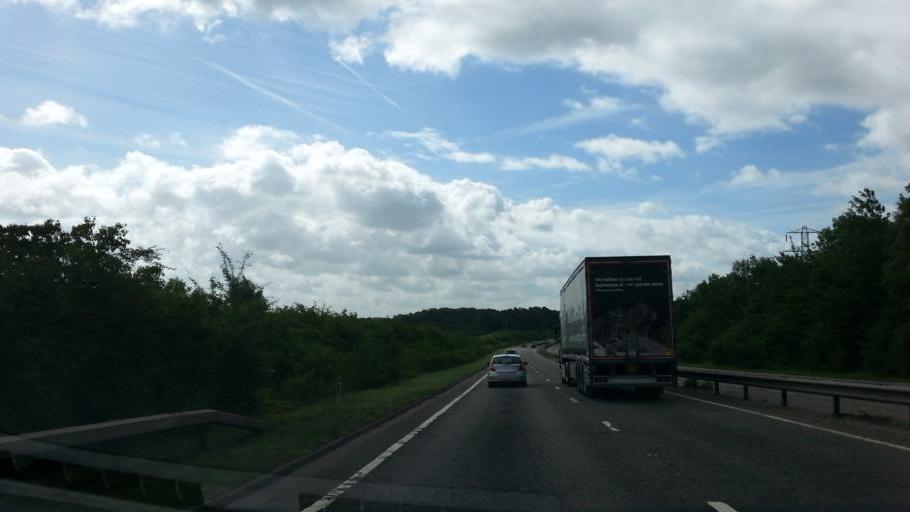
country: GB
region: England
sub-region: Warwickshire
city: Ryton on Dunsmore
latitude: 52.4049
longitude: -1.4336
